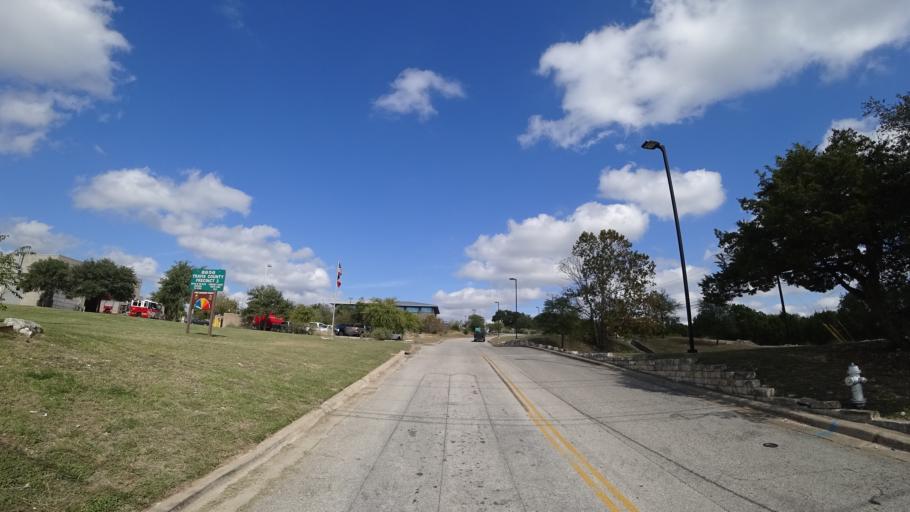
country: US
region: Texas
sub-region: Travis County
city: Barton Creek
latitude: 30.2500
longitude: -97.8942
